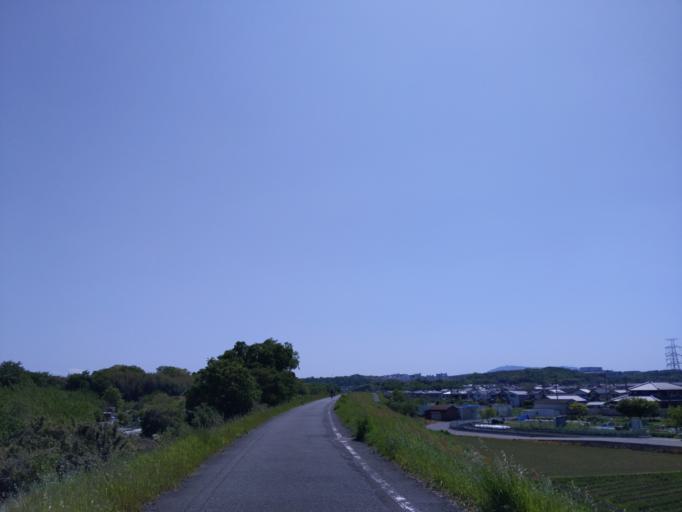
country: JP
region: Nara
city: Nara-shi
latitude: 34.7566
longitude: 135.8031
